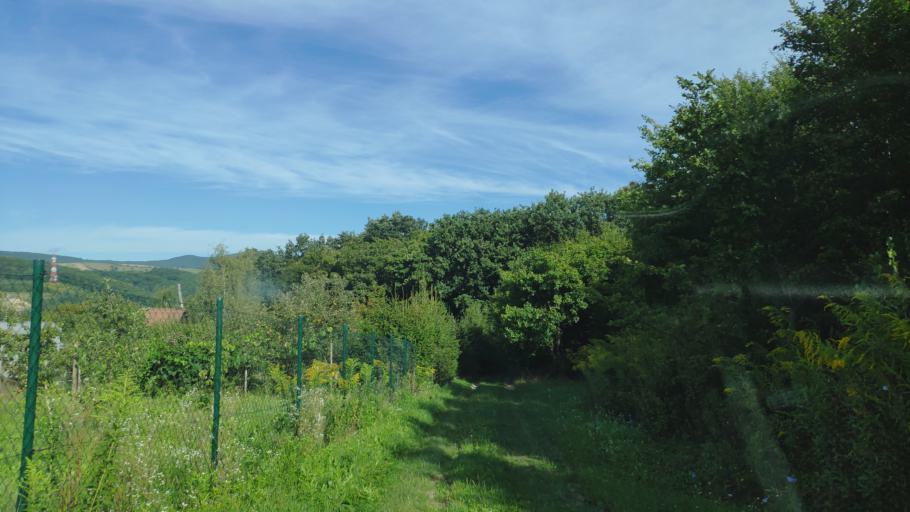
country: SK
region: Kosicky
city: Kosice
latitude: 48.7680
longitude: 21.2493
